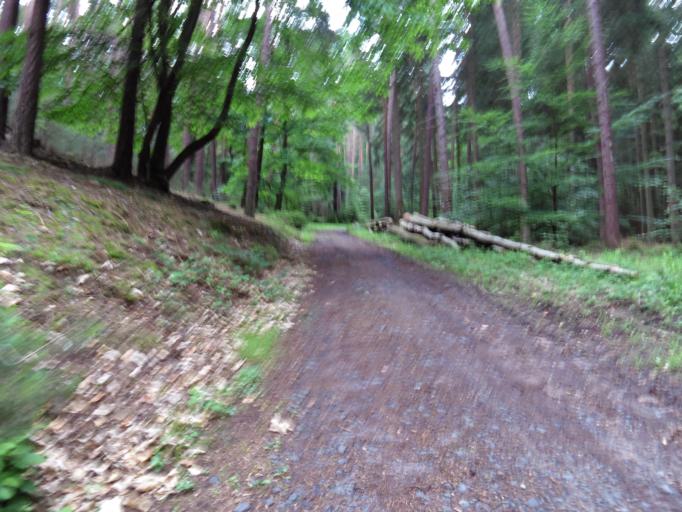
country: DE
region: Rheinland-Pfalz
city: Weisenheim am Berg
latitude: 49.5060
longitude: 8.1212
